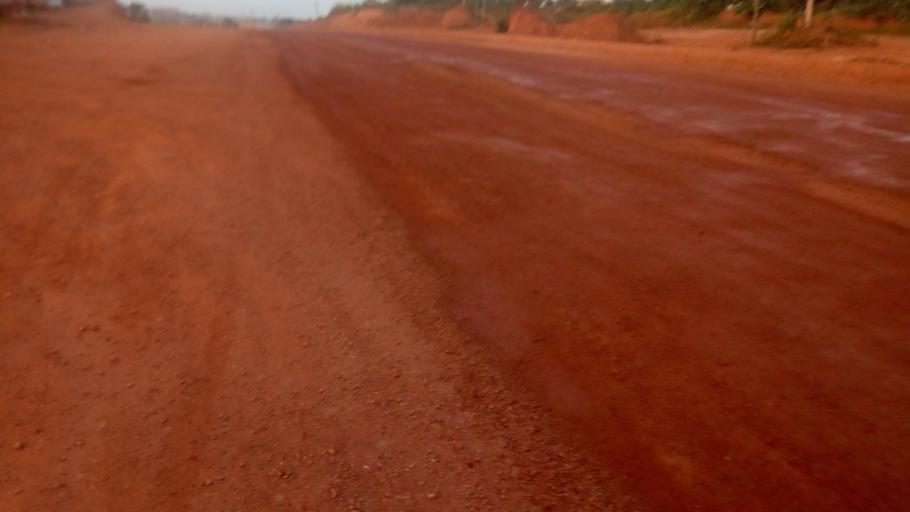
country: GH
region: Ashanti
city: Obuasi
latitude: 6.2225
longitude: -1.6843
